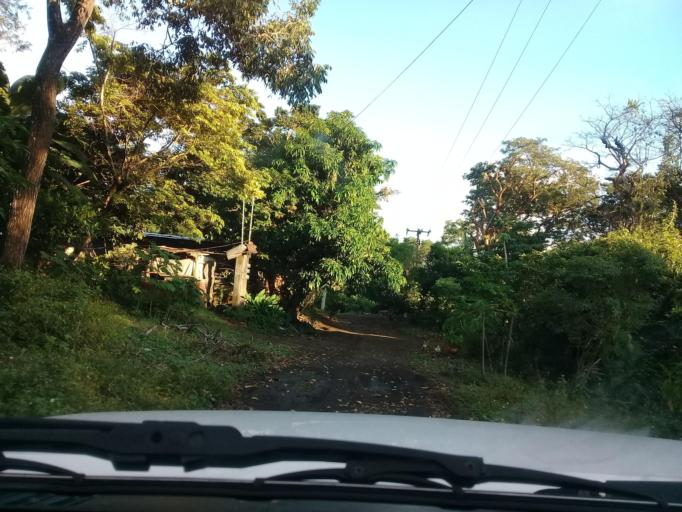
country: MX
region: Veracruz
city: Catemaco
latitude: 18.4309
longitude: -95.0893
